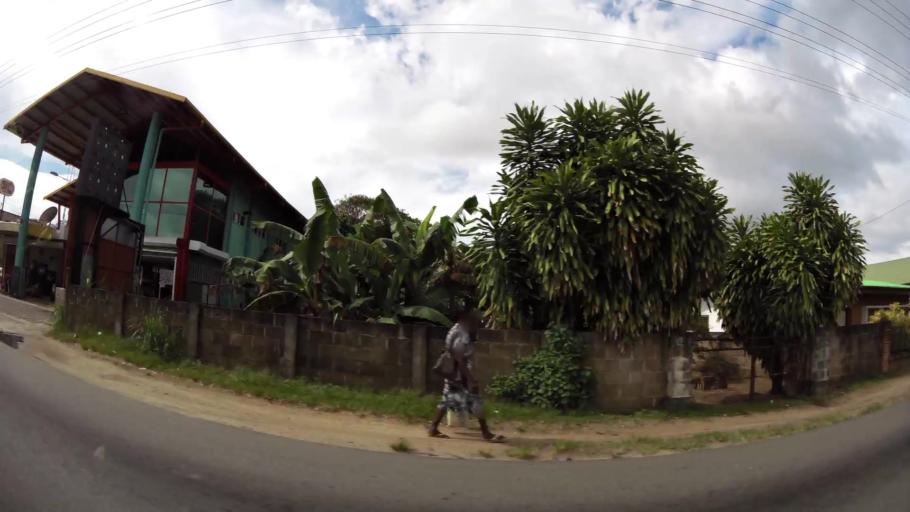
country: SR
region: Paramaribo
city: Paramaribo
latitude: 5.8405
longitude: -55.1867
